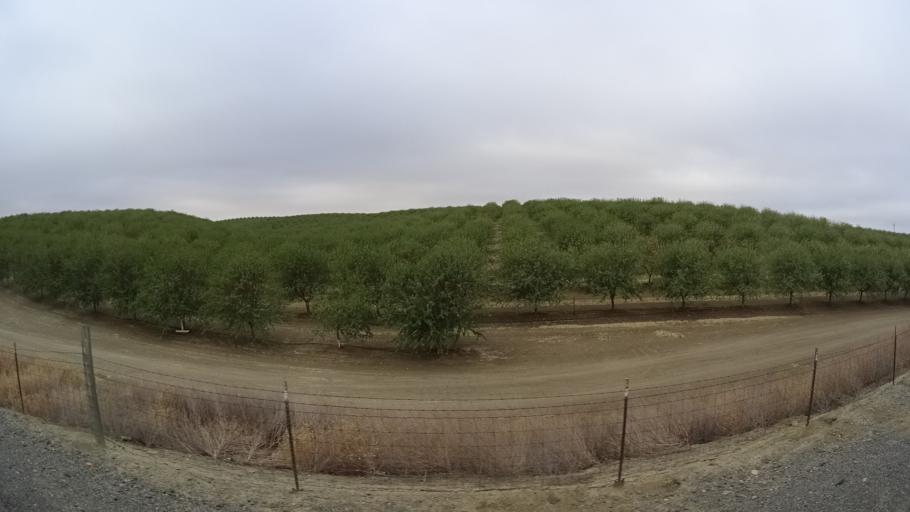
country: US
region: California
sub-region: Yolo County
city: Dunnigan
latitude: 38.8843
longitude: -122.0261
